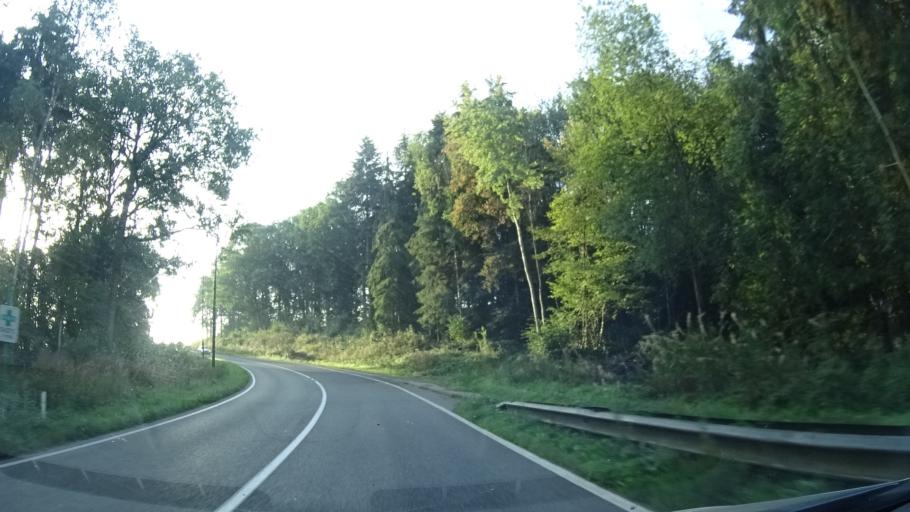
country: BE
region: Wallonia
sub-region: Province de Namur
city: Cerfontaine
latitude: 50.1950
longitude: 4.3783
